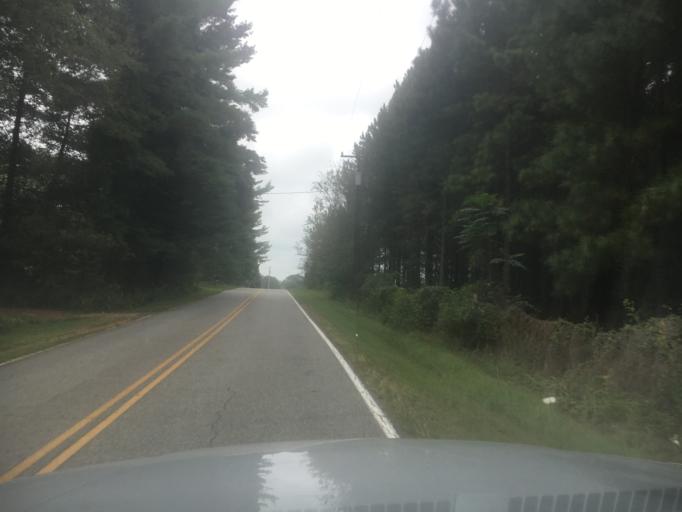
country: US
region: South Carolina
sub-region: Spartanburg County
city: Landrum
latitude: 35.1640
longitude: -82.0907
